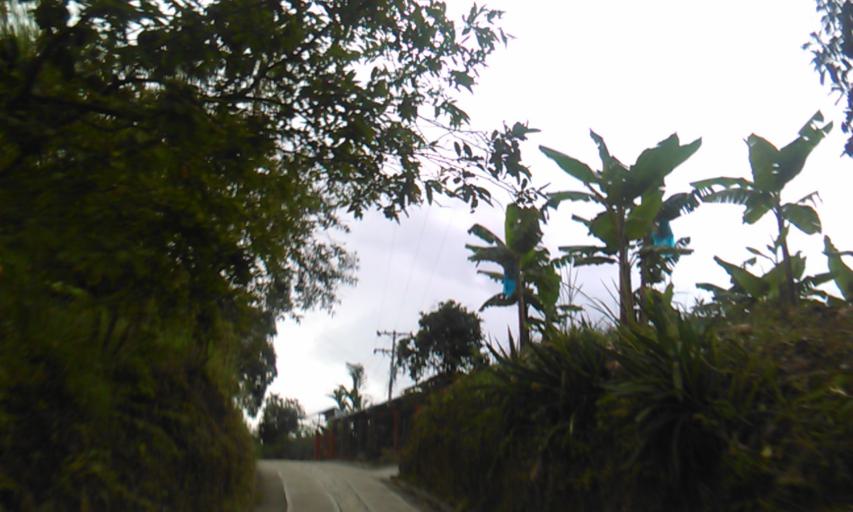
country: CO
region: Quindio
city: Cordoba
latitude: 4.4122
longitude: -75.6821
